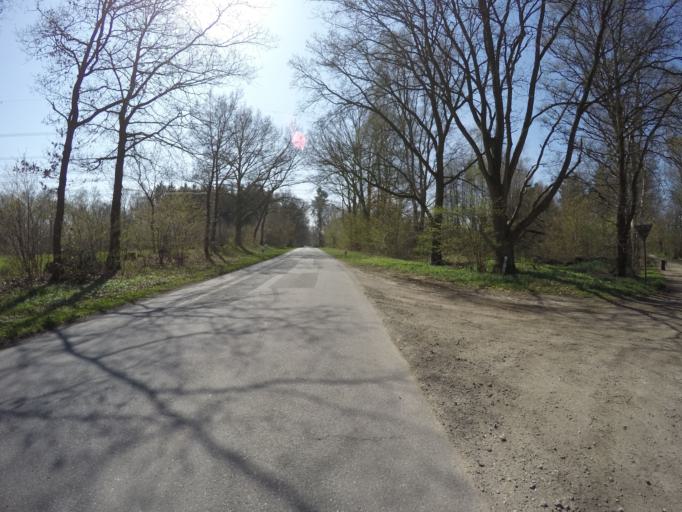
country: DE
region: Schleswig-Holstein
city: Quickborn
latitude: 53.7211
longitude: 9.9242
